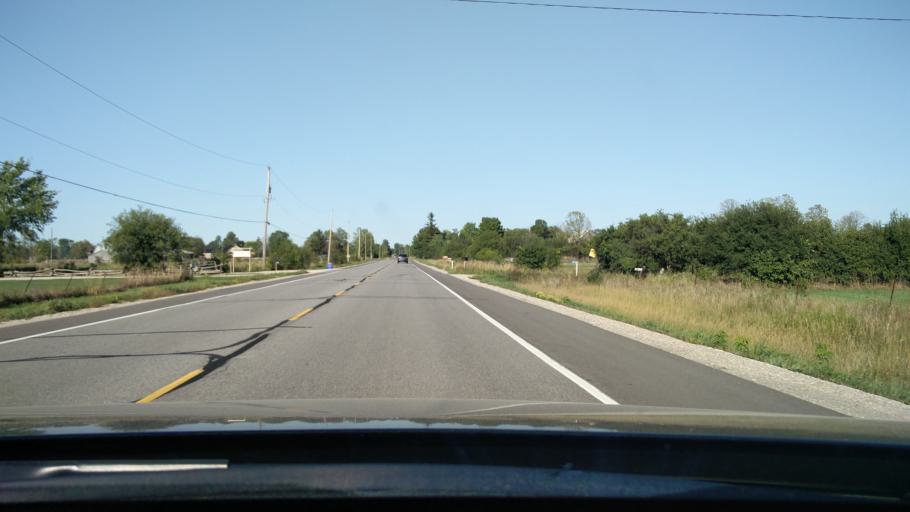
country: CA
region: Ontario
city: Perth
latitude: 44.9550
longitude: -76.1622
